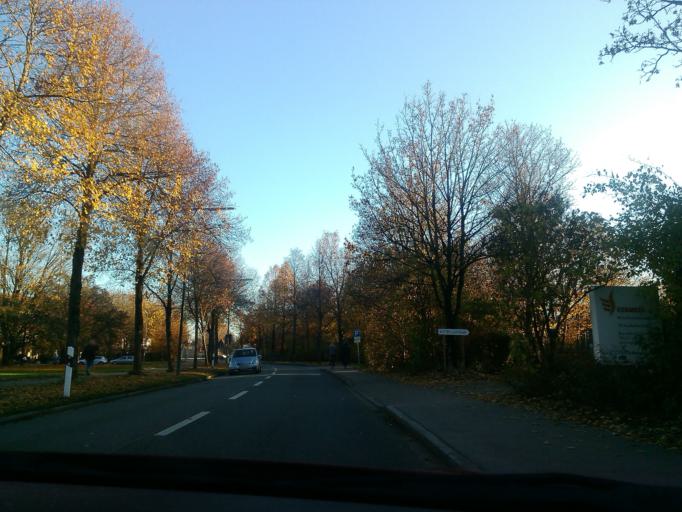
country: DE
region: Bavaria
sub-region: Upper Bavaria
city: Pasing
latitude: 48.1369
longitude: 11.4616
